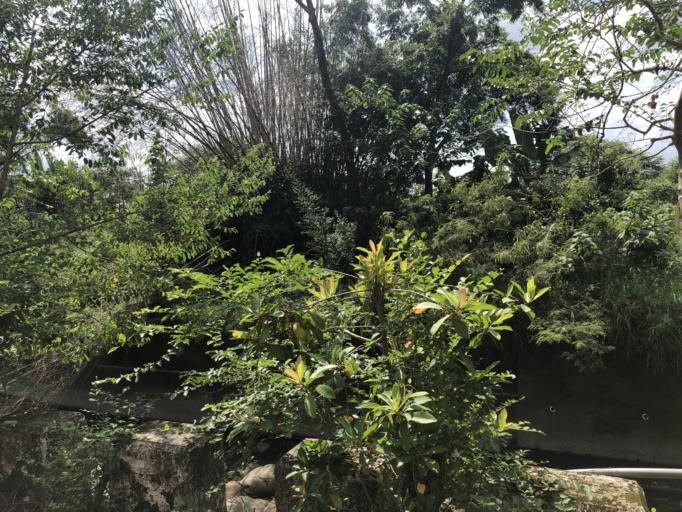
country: TW
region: Taiwan
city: Yujing
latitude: 22.9335
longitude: 120.5875
